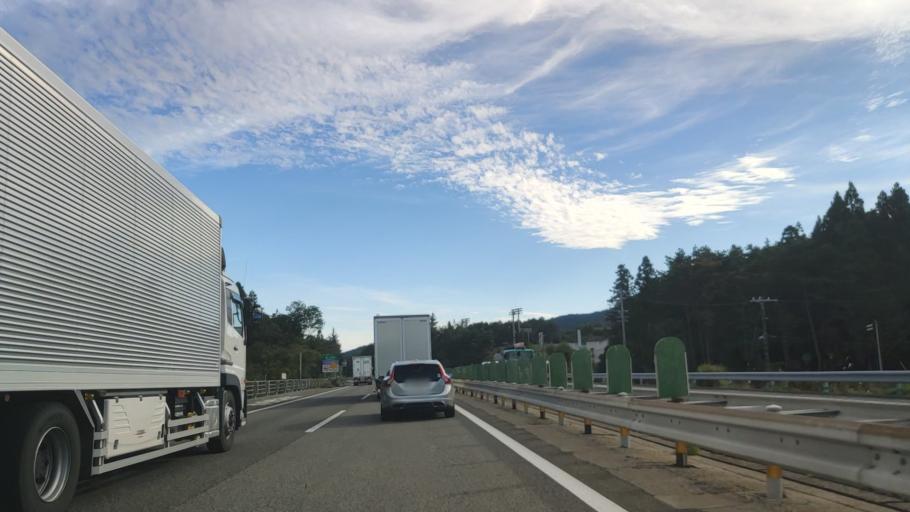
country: JP
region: Nagano
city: Ina
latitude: 35.7184
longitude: 137.9071
